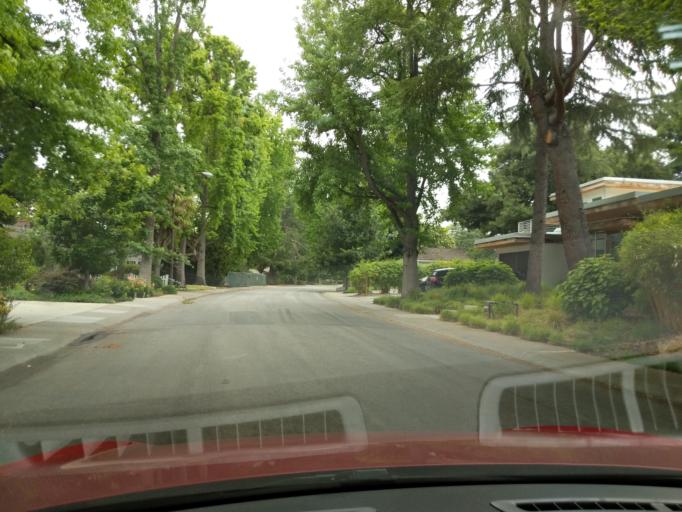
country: US
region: California
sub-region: San Mateo County
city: Menlo Park
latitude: 37.4492
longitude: -122.1685
